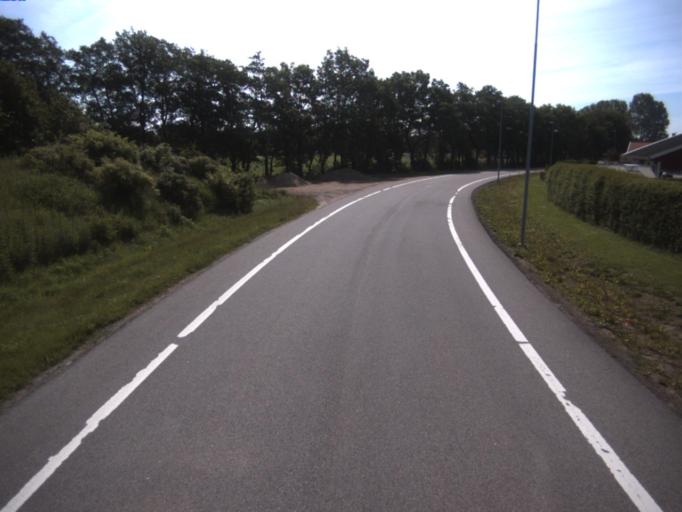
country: SE
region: Skane
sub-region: Helsingborg
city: Odakra
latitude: 56.0487
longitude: 12.7512
